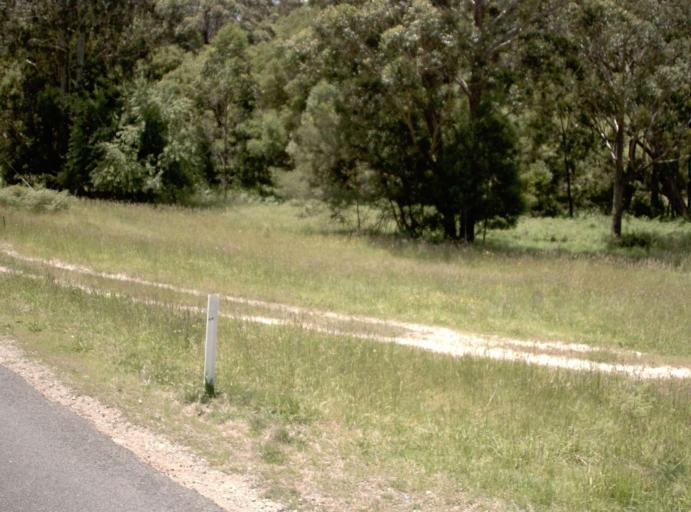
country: AU
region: New South Wales
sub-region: Bombala
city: Bombala
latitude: -37.5412
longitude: 148.9371
